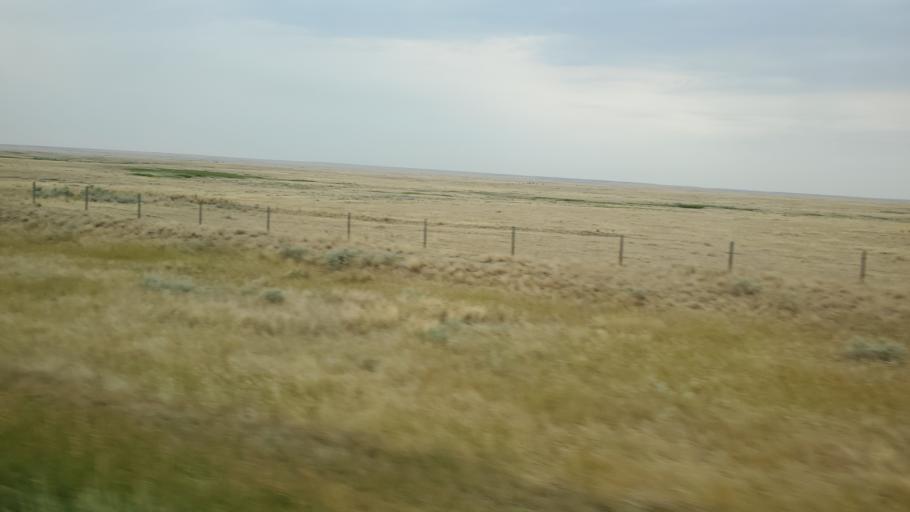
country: US
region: Montana
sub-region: Hill County
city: Havre
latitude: 49.1955
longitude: -110.2522
